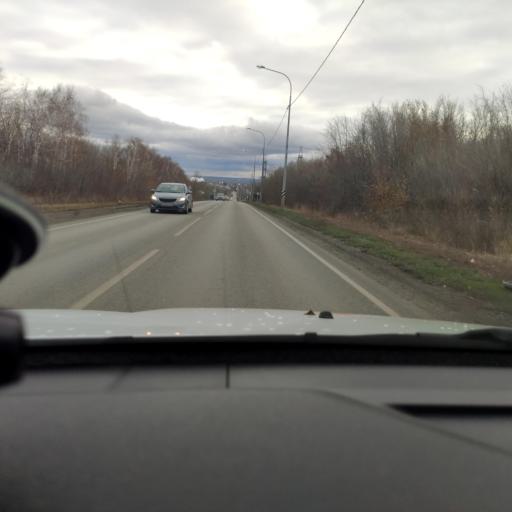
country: RU
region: Samara
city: Petra-Dubrava
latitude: 53.2785
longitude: 50.3798
